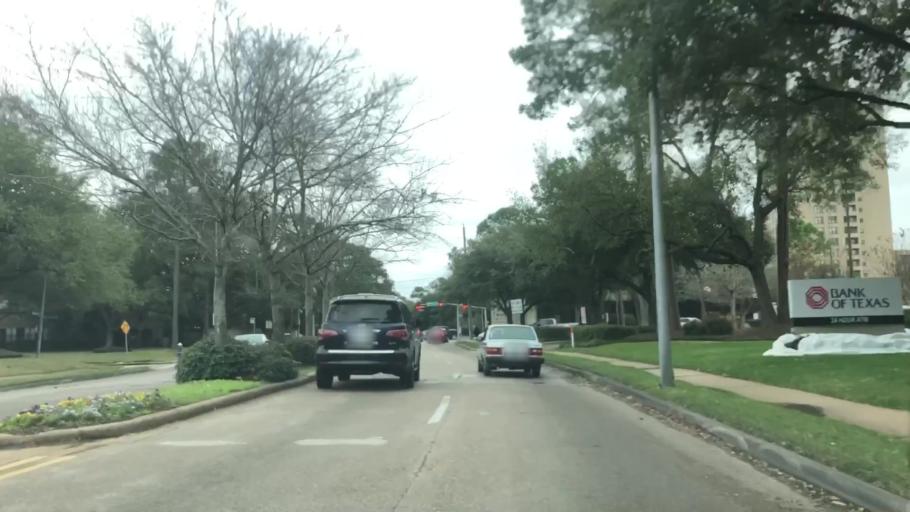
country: US
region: Texas
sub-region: Harris County
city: Hunters Creek Village
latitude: 29.7650
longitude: -95.4783
